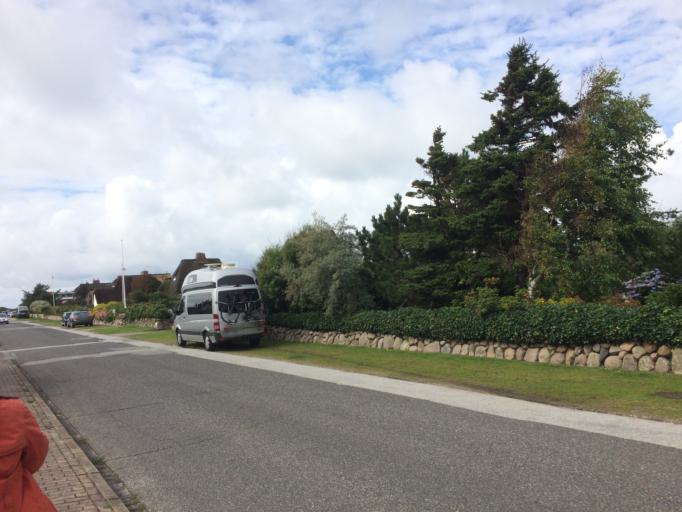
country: DE
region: Schleswig-Holstein
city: Westerland
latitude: 54.9305
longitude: 8.3177
